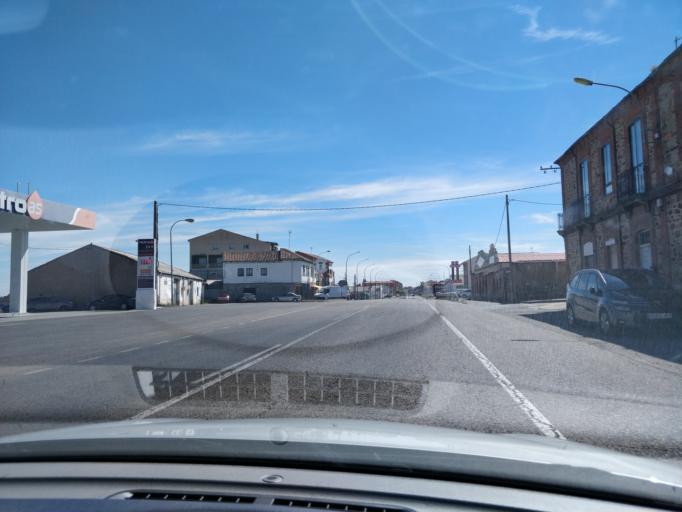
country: ES
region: Castille and Leon
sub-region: Provincia de Leon
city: Astorga
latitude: 42.4654
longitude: -6.0745
